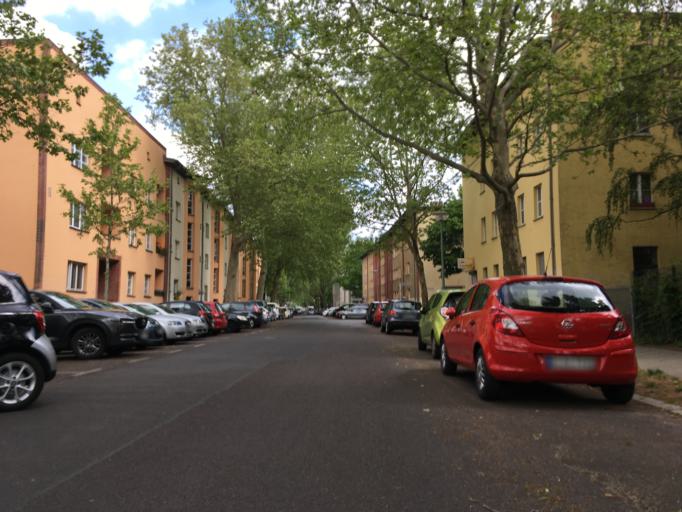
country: DE
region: Berlin
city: Friedrichsfelde
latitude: 52.5059
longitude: 13.5074
